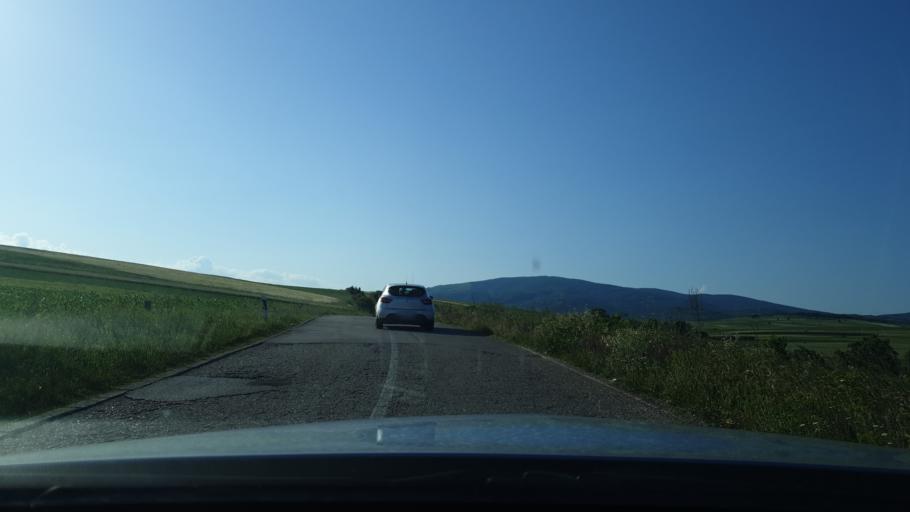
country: RS
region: Central Serbia
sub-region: Nisavski Okrug
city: Aleksinac
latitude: 43.6199
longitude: 21.6799
